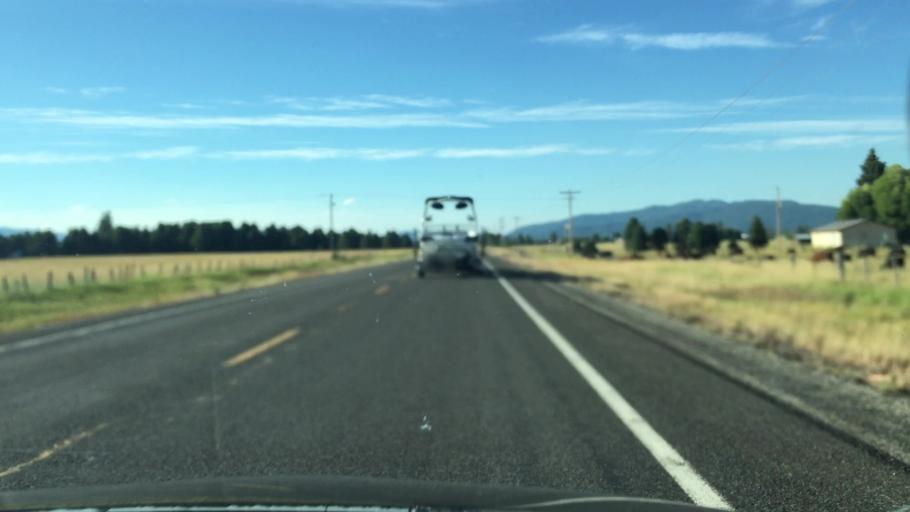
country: US
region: Idaho
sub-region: Valley County
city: Cascade
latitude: 44.4430
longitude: -115.9994
